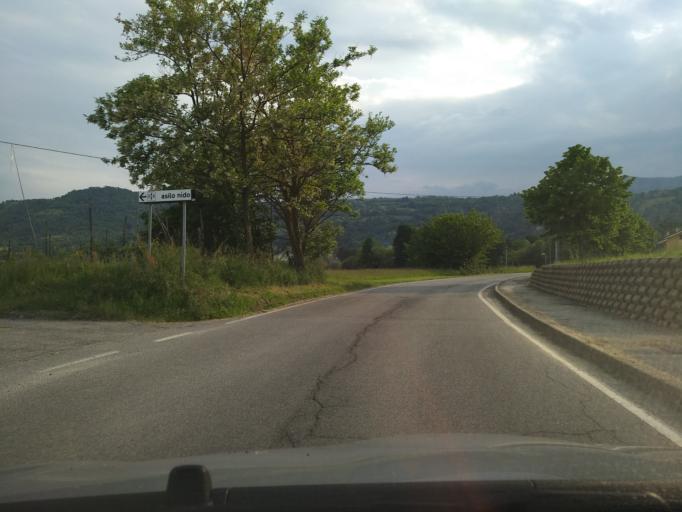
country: IT
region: Piedmont
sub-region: Provincia di Torino
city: Roletto
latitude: 44.9201
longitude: 7.3384
